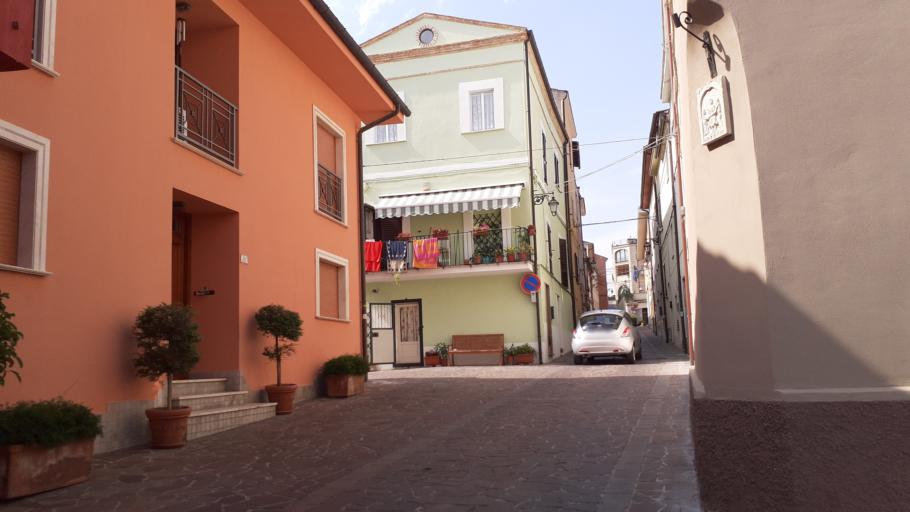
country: IT
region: Abruzzo
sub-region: Provincia di Chieti
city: Vacri
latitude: 42.2983
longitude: 14.2335
